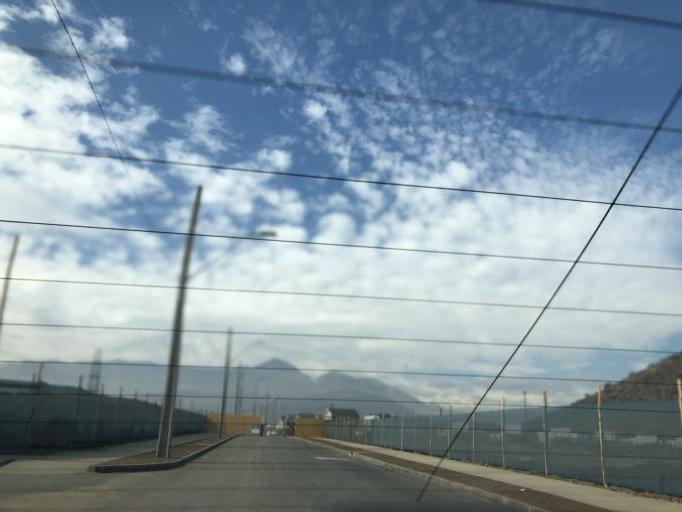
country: CL
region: Santiago Metropolitan
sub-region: Provincia de Cordillera
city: Puente Alto
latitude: -33.6014
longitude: -70.5454
